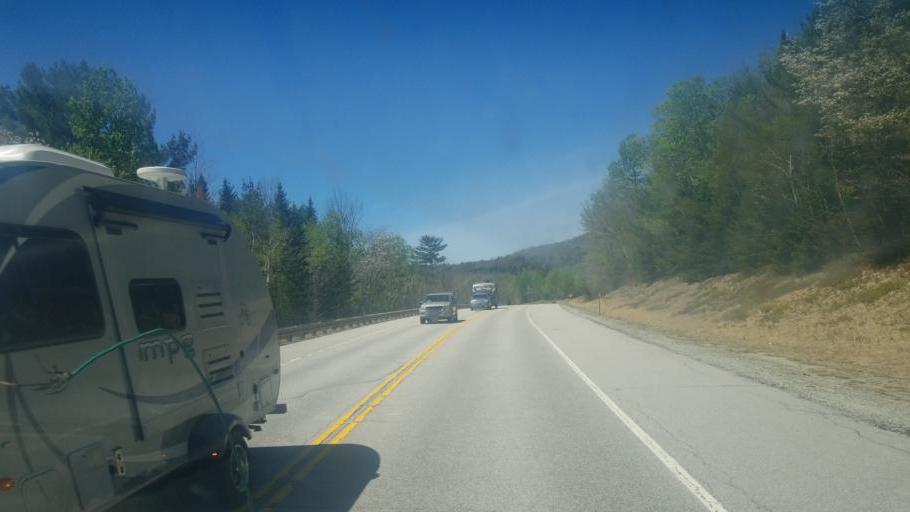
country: US
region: New Hampshire
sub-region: Grafton County
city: Deerfield
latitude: 44.2704
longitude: -71.5107
